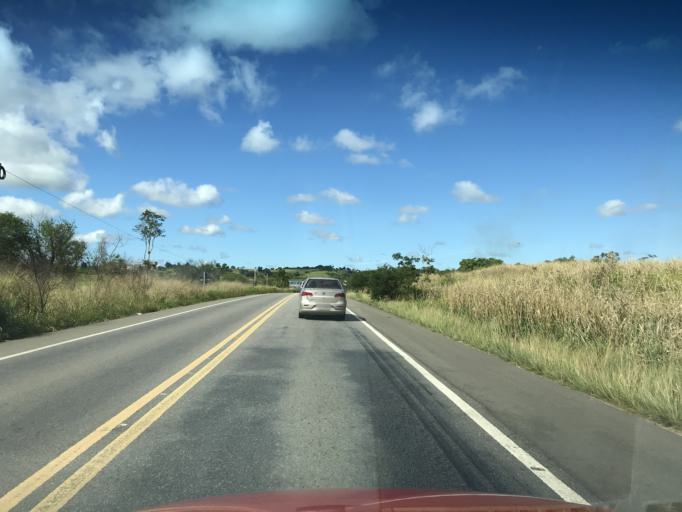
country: BR
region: Bahia
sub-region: Conceicao Do Almeida
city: Muritiba
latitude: -12.9378
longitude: -39.2520
